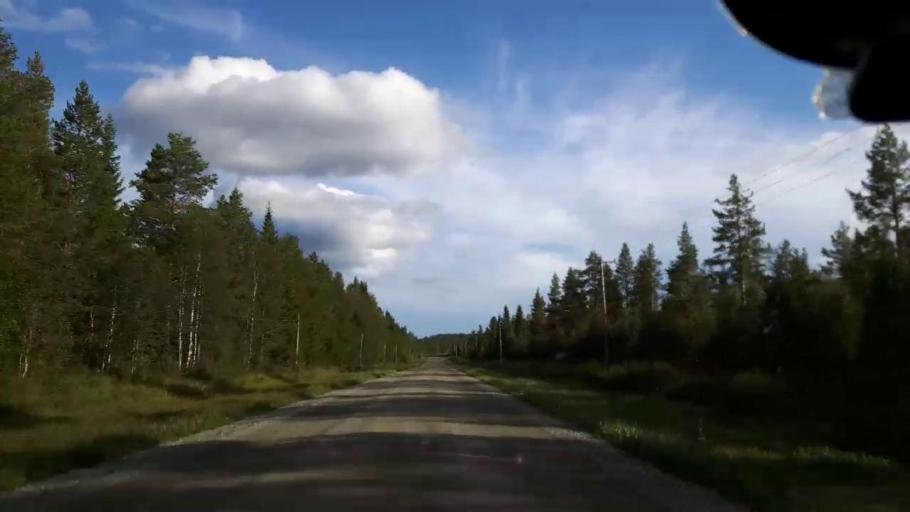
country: SE
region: Jaemtland
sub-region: Stroemsunds Kommun
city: Stroemsund
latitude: 63.3041
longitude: 15.5553
